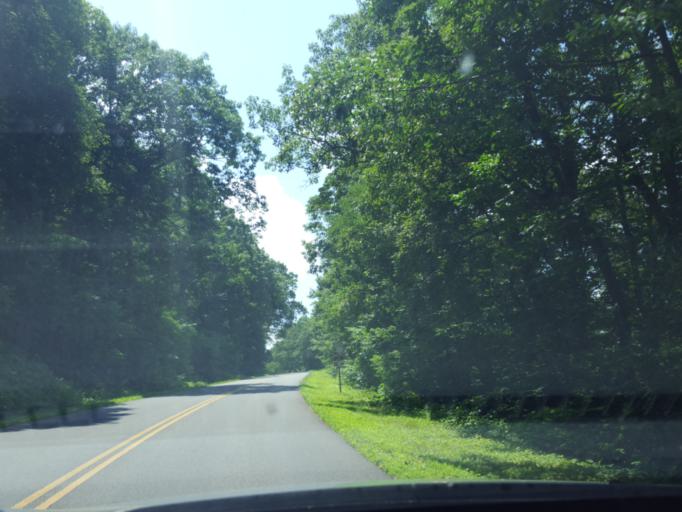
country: US
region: Virginia
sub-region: Nelson County
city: Nellysford
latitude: 37.9350
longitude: -78.9502
